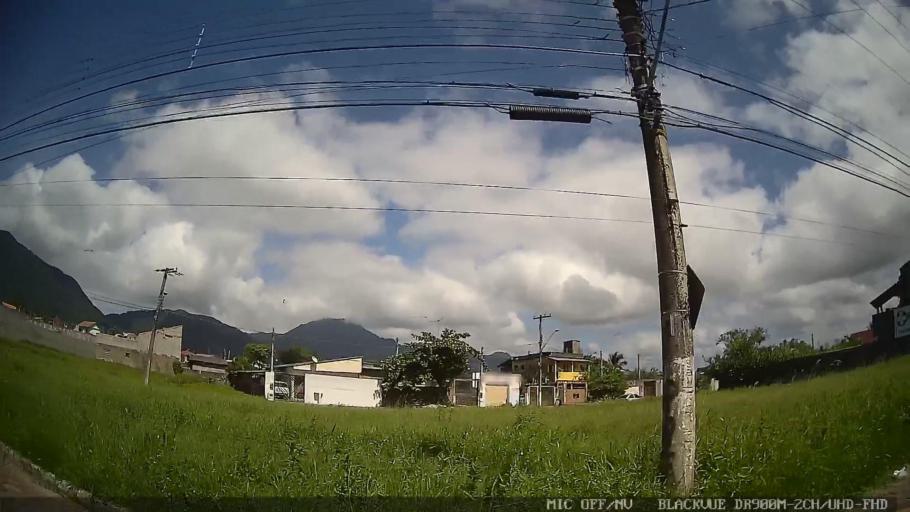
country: BR
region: Sao Paulo
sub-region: Peruibe
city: Peruibe
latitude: -24.3146
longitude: -47.0095
